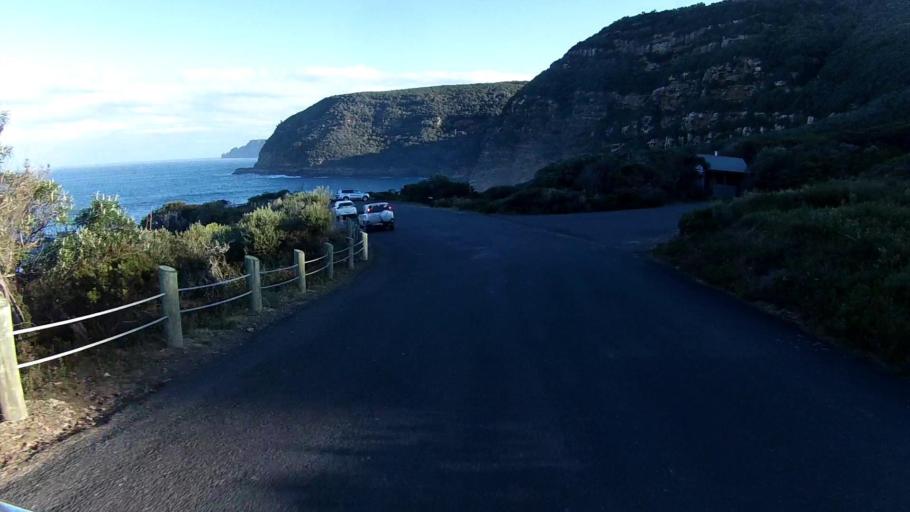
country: AU
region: Tasmania
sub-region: Clarence
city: Sandford
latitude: -43.1872
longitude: 147.8461
